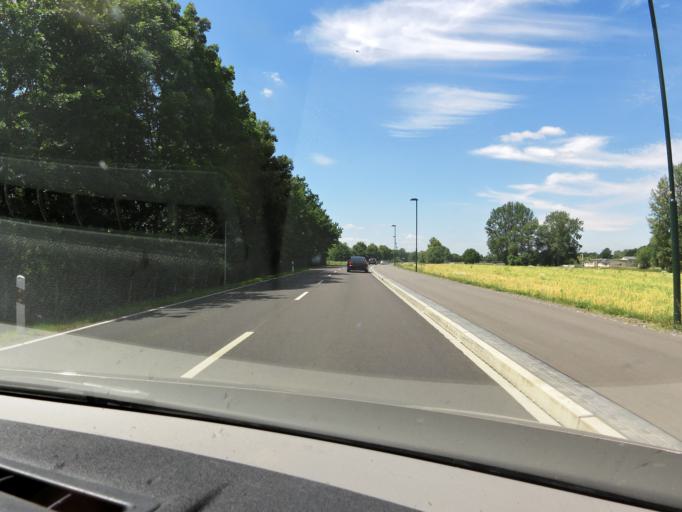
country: DE
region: Saxony-Anhalt
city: Zoschen
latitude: 51.3567
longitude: 12.1138
